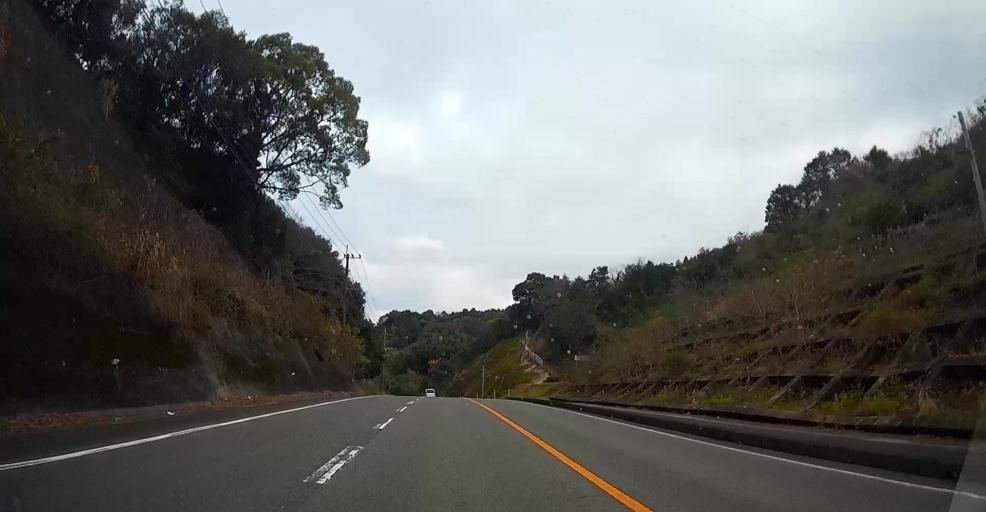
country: JP
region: Kumamoto
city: Hondo
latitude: 32.4944
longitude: 130.2978
